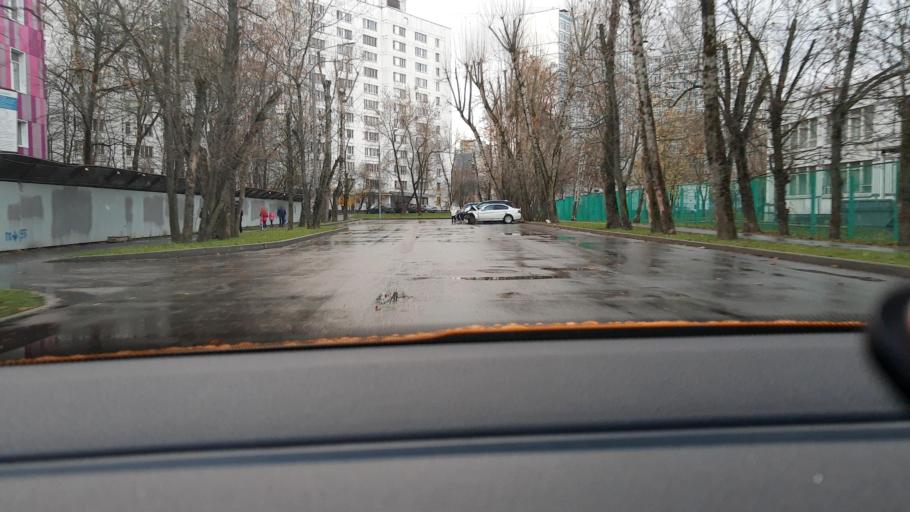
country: RU
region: Moscow
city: Vatutino
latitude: 55.8840
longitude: 37.6959
